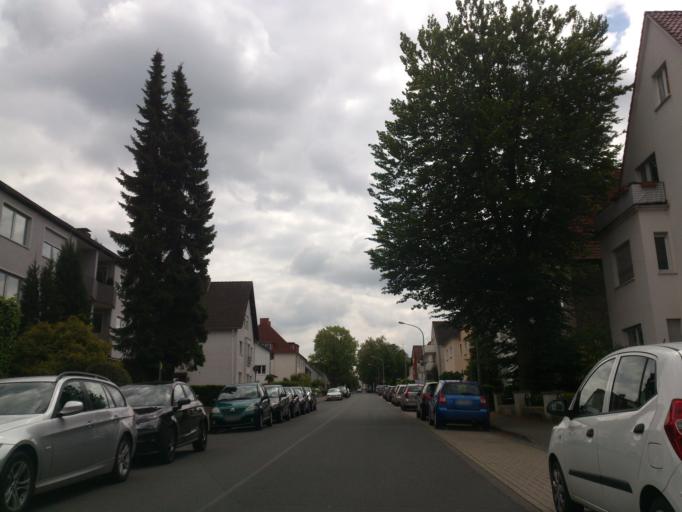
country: DE
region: North Rhine-Westphalia
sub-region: Regierungsbezirk Detmold
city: Paderborn
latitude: 51.7105
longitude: 8.7560
